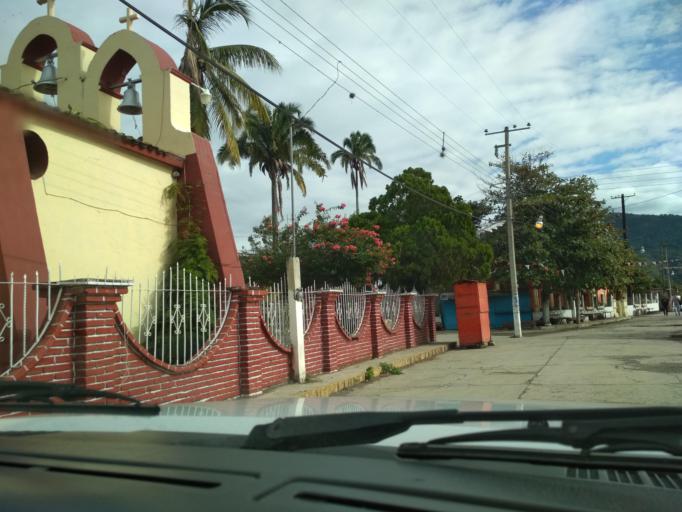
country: MX
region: Veracruz
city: Alto Lucero
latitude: 19.5903
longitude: -96.7833
